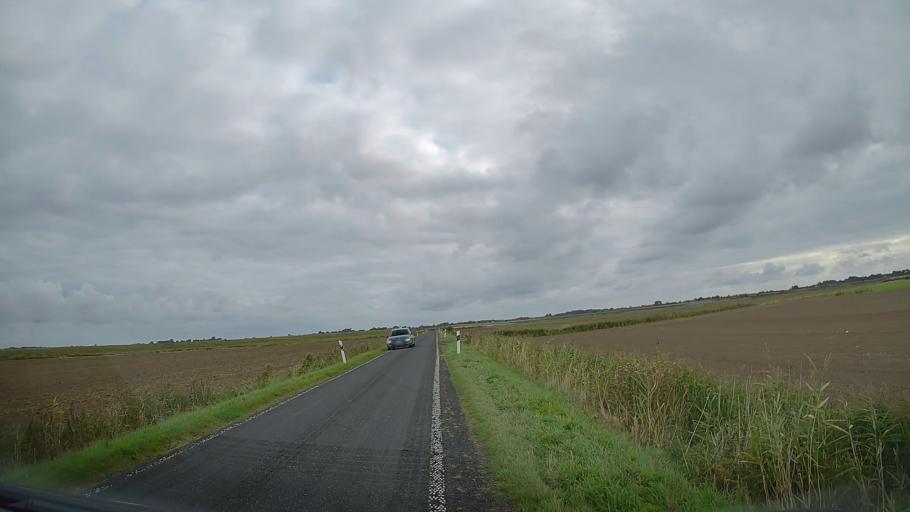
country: DE
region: Schleswig-Holstein
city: Rodenas
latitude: 54.8924
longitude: 8.7208
